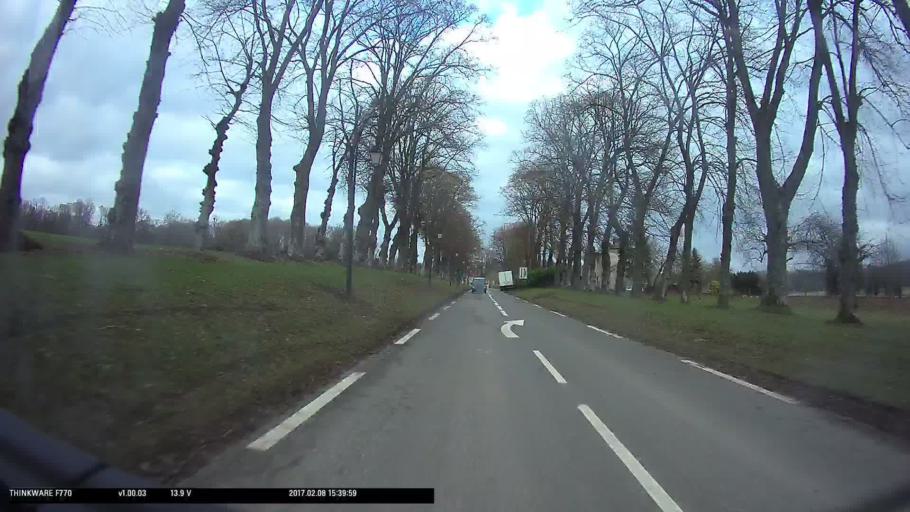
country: FR
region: Ile-de-France
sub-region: Departement du Val-d'Oise
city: Vigny
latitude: 49.0717
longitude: 1.9236
